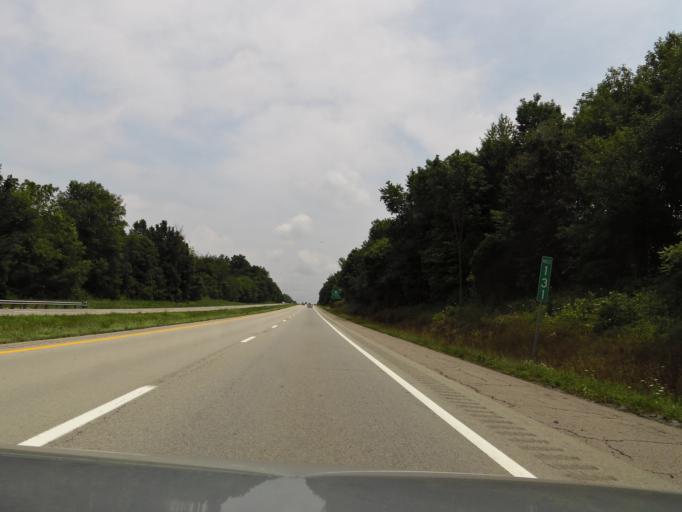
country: US
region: Kentucky
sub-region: Hardin County
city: Elizabethtown
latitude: 37.6368
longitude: -85.9276
